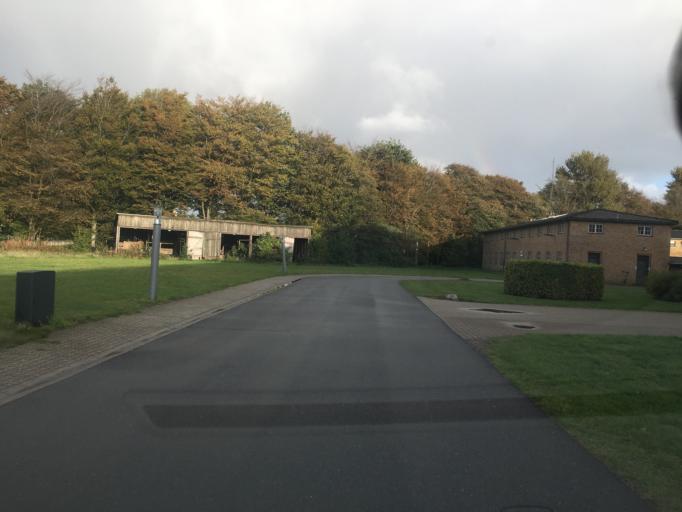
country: DK
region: South Denmark
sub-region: Tonder Kommune
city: Tonder
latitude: 54.9499
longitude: 8.8804
